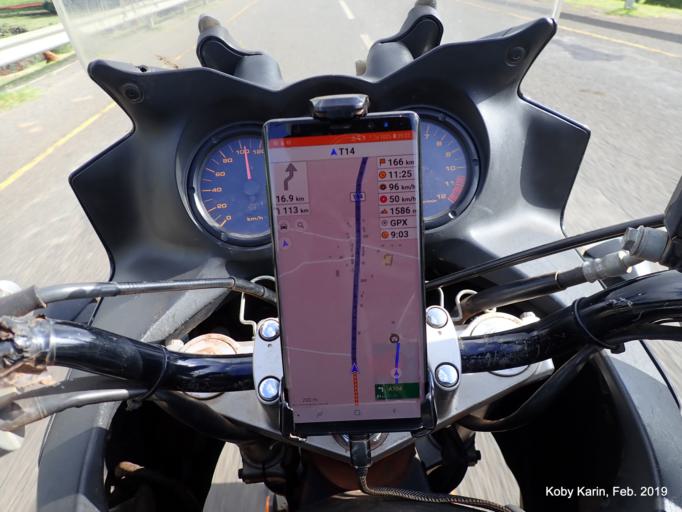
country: TZ
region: Manyara
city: Endasak
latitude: -4.3618
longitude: 35.5558
